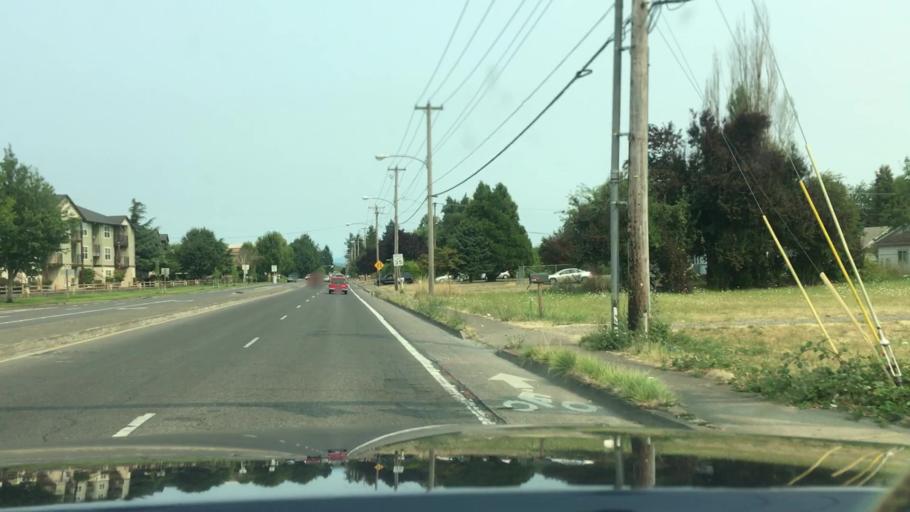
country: US
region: Oregon
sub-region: Lane County
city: Eugene
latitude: 44.0845
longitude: -123.1679
